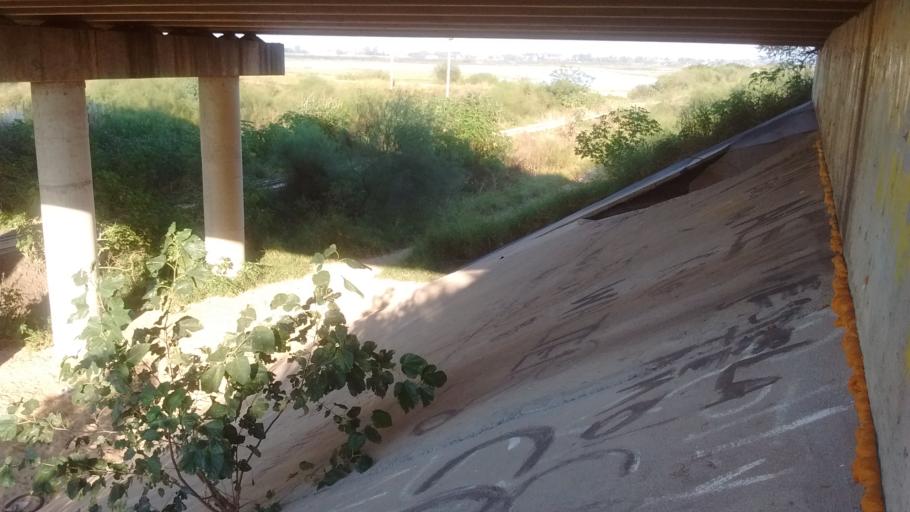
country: AR
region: Santa Fe
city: Santo Tome
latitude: -31.6539
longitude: -60.7398
